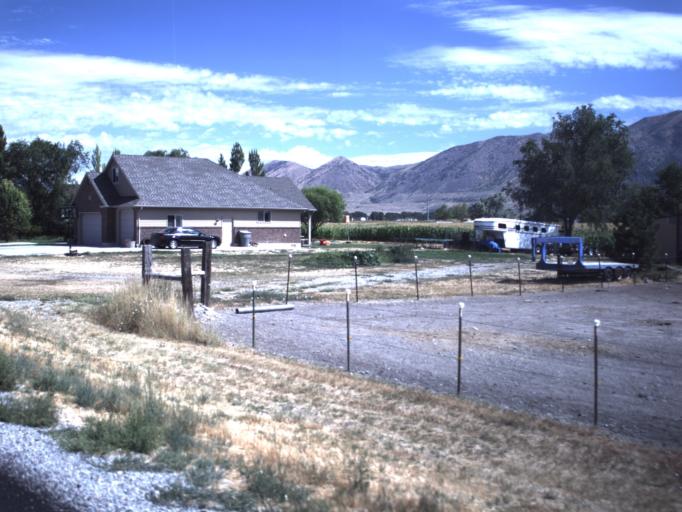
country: US
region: Utah
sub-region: Box Elder County
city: Elwood
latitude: 41.6612
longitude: -112.1406
